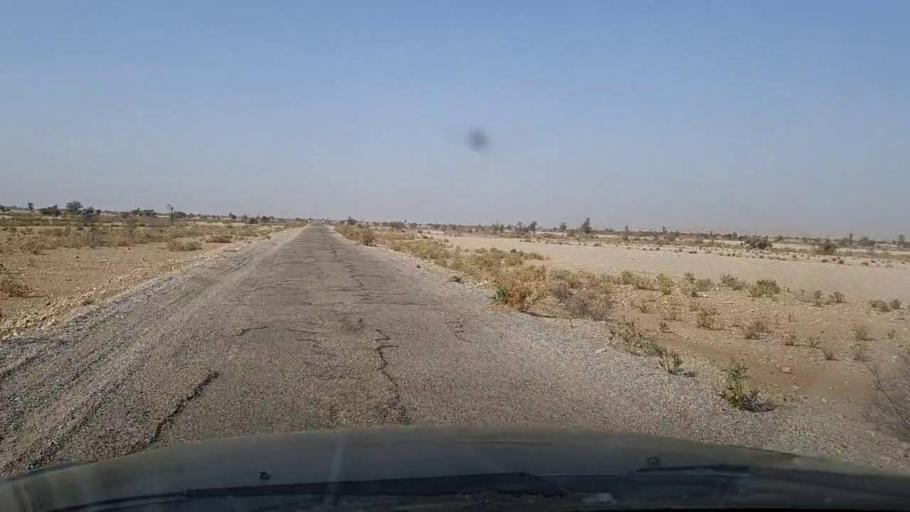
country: PK
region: Sindh
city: Sann
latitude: 25.9163
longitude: 68.0119
